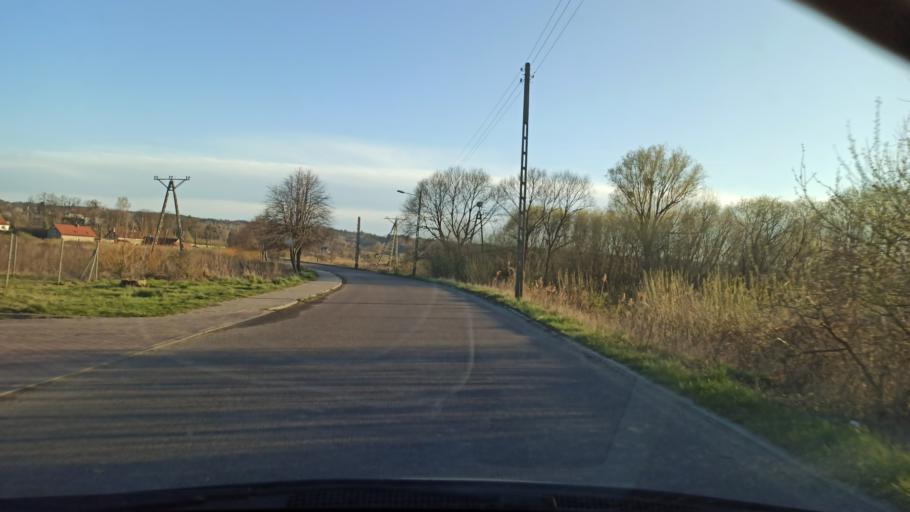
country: PL
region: Warmian-Masurian Voivodeship
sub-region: Powiat elblaski
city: Tolkmicko
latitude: 54.3198
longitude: 19.5219
